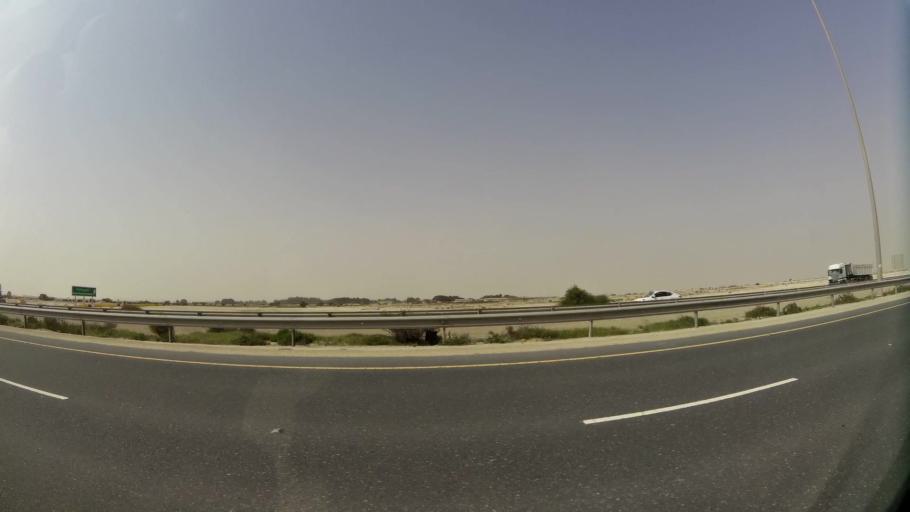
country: QA
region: Baladiyat ar Rayyan
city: Ar Rayyan
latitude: 25.1574
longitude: 51.2863
